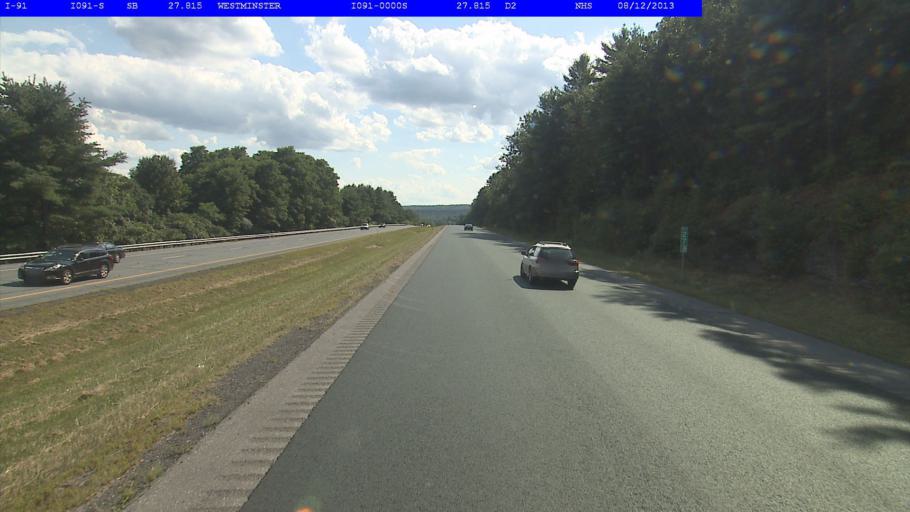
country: US
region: Vermont
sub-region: Windham County
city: Bellows Falls
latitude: 43.0808
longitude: -72.4633
